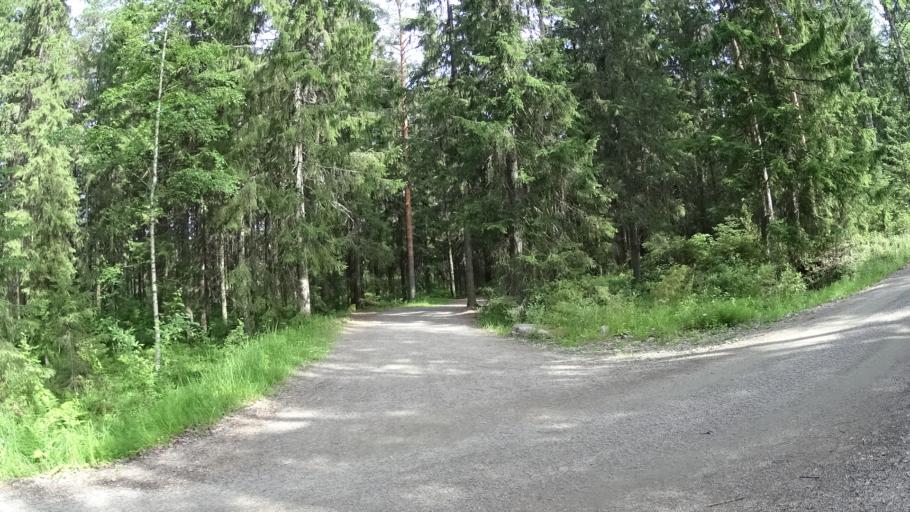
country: FI
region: Southern Ostrobothnia
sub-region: Kuusiokunnat
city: AEhtaeri
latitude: 62.5387
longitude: 24.1788
